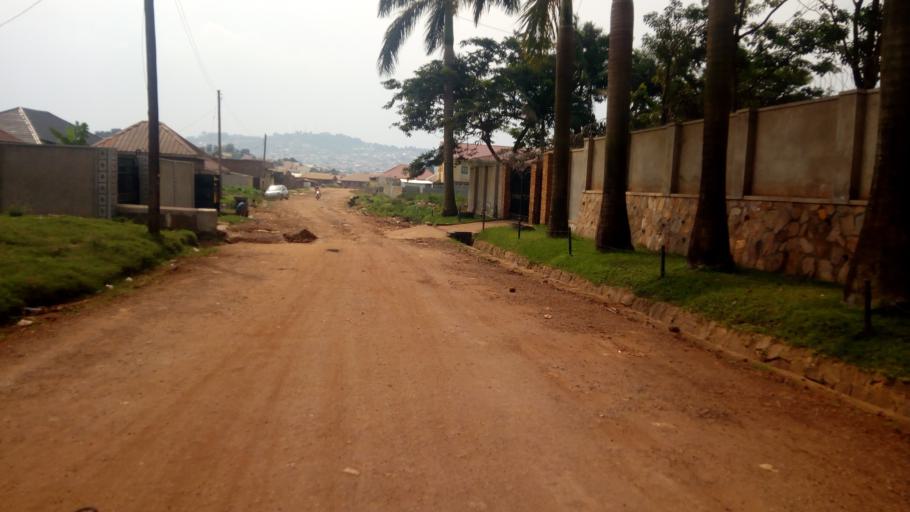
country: UG
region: Central Region
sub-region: Wakiso District
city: Kireka
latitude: 0.3176
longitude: 32.6529
